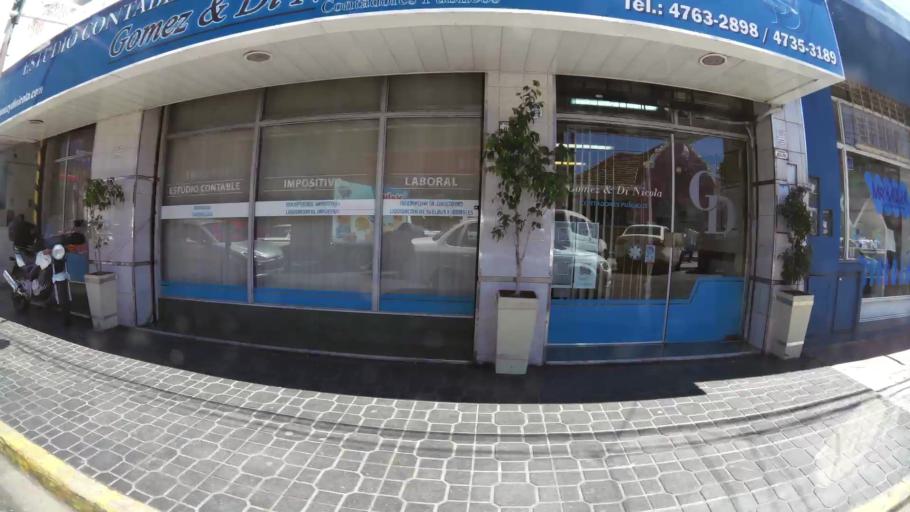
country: AR
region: Buenos Aires
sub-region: Partido de General San Martin
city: General San Martin
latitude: -34.5266
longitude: -58.5497
